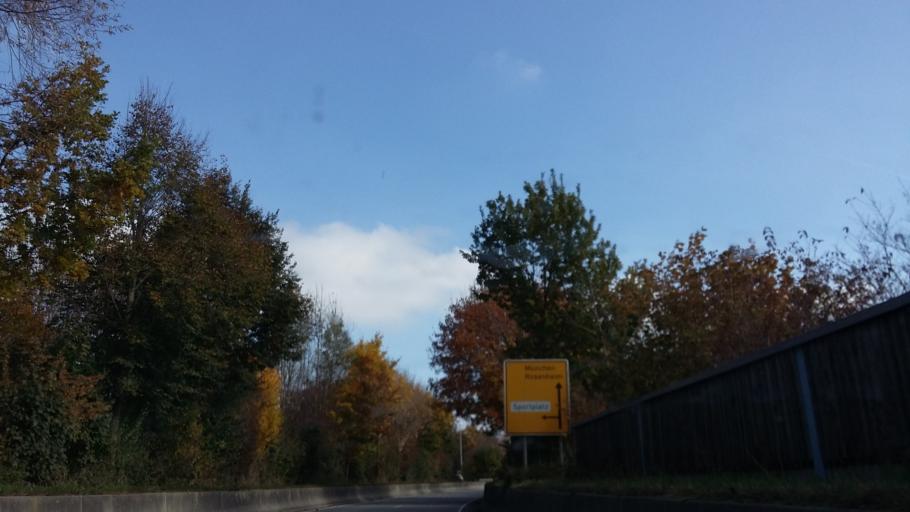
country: DE
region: Bavaria
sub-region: Upper Bavaria
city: Bad Aibling
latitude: 47.8595
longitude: 11.9791
